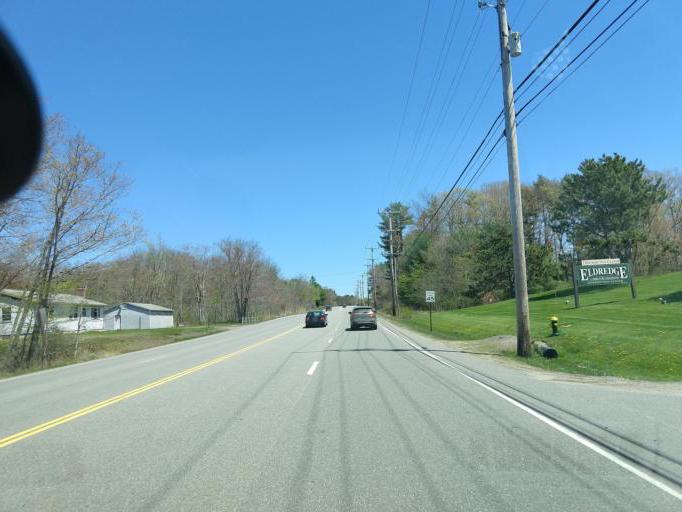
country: US
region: Maine
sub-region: York County
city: York Harbor
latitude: 43.1606
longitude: -70.6495
